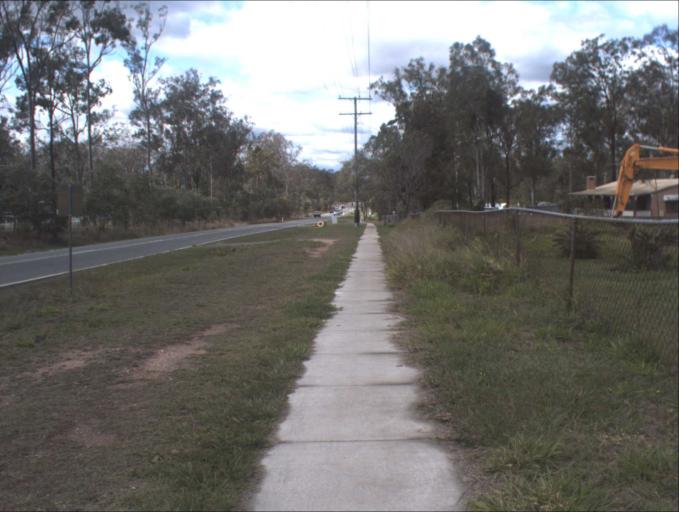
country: AU
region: Queensland
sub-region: Logan
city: Park Ridge South
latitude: -27.7146
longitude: 152.9785
